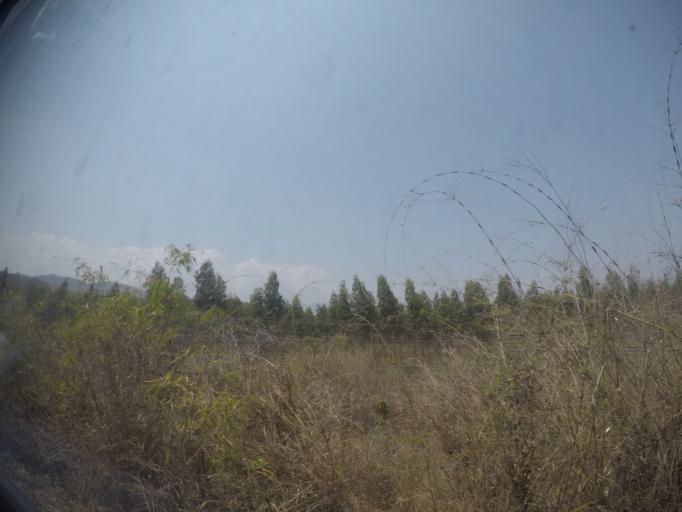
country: VN
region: Binh Thuan
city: Thuan Nam
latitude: 10.9272
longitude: 107.9011
